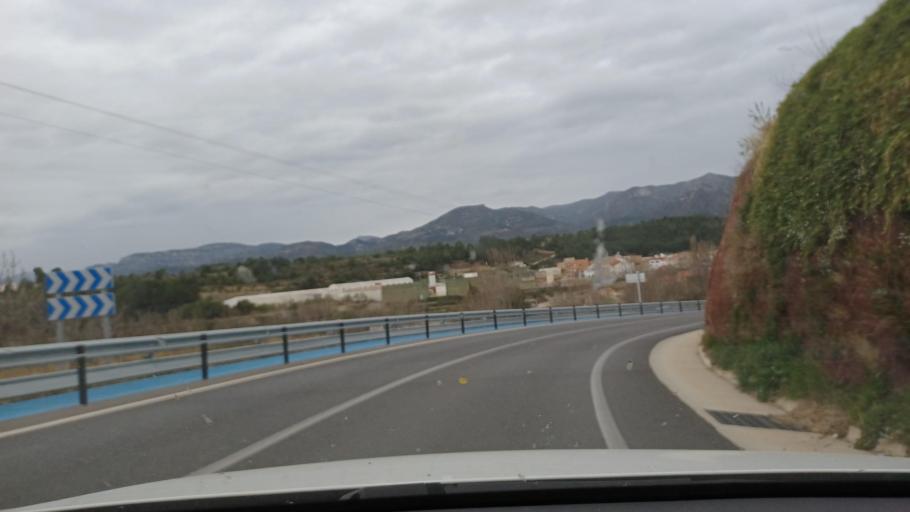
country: ES
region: Valencia
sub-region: Provincia de Castello
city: Rosell
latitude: 40.6320
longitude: 0.2803
